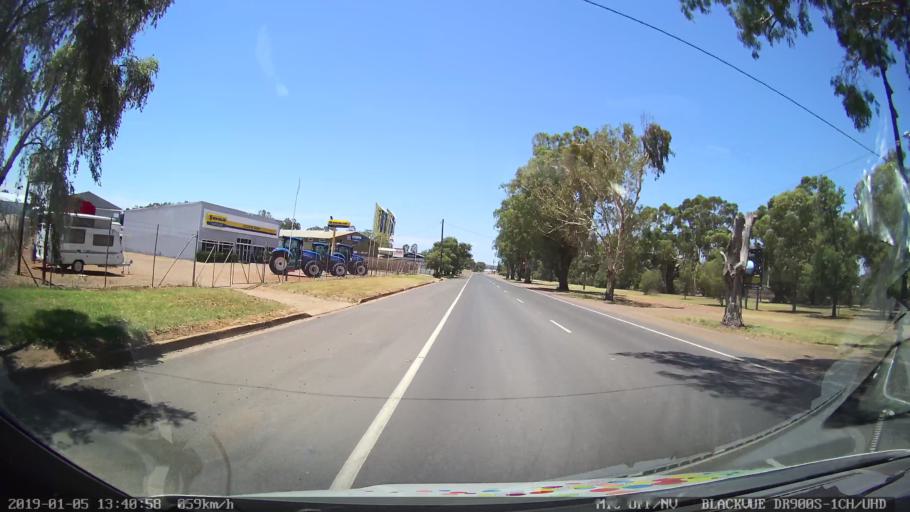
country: AU
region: New South Wales
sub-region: Gunnedah
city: Gunnedah
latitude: -30.9799
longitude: 150.2352
